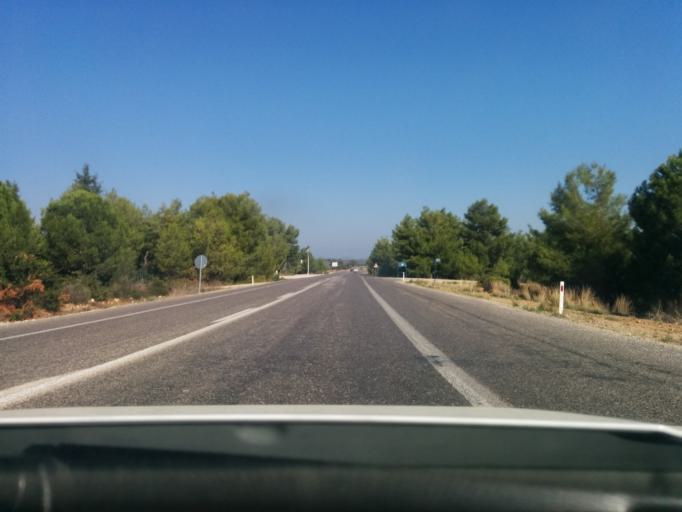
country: TR
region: Mugla
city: Esen
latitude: 36.3797
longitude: 29.3222
